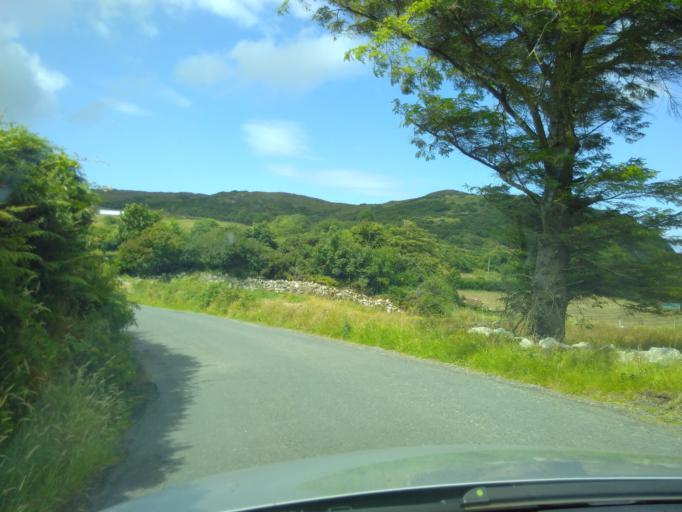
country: IE
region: Ulster
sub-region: County Donegal
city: Ramelton
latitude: 55.2235
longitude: -7.6236
